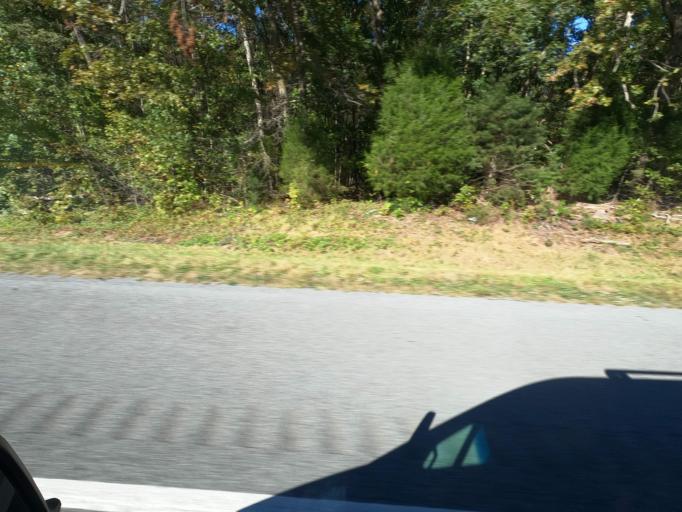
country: US
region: Tennessee
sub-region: Cheatham County
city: Kingston Springs
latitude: 36.0528
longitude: -87.1412
